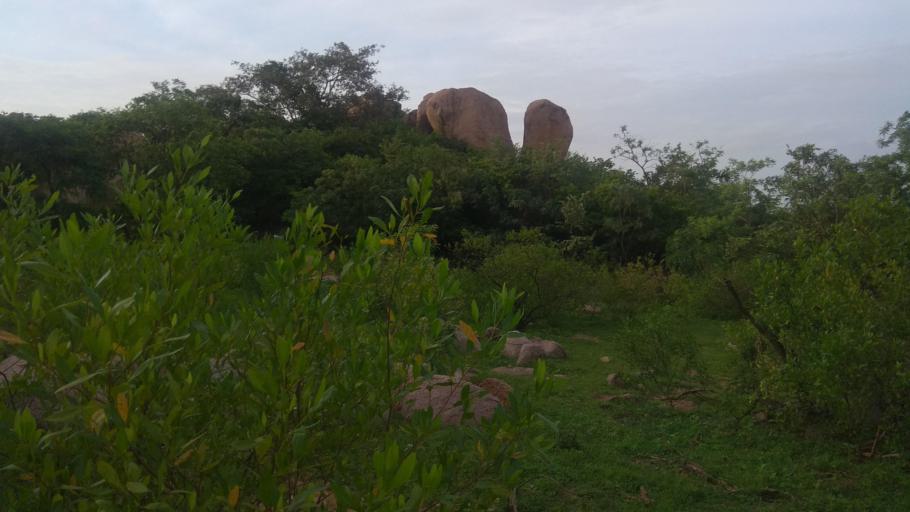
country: IN
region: Telangana
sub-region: Mahbubnagar
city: Farrukhnagar
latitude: 16.8965
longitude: 78.4952
